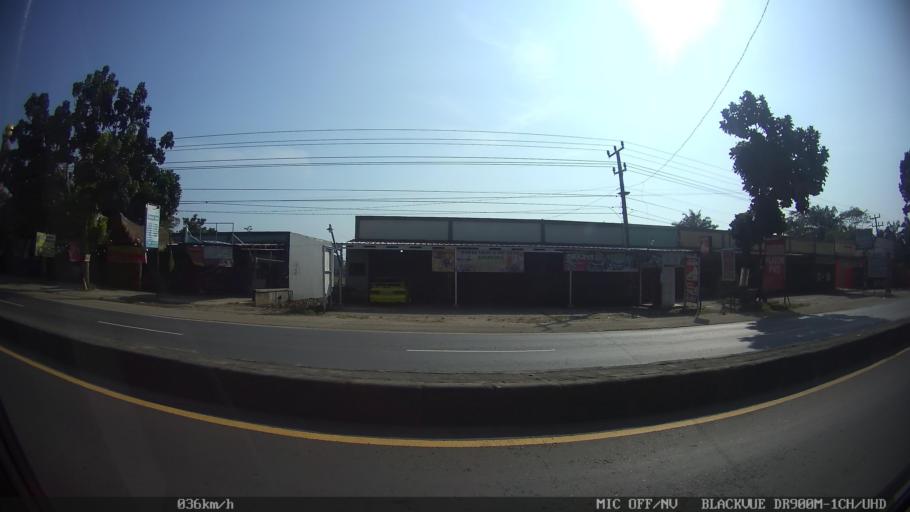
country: ID
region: Lampung
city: Natar
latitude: -5.3262
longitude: 105.2021
